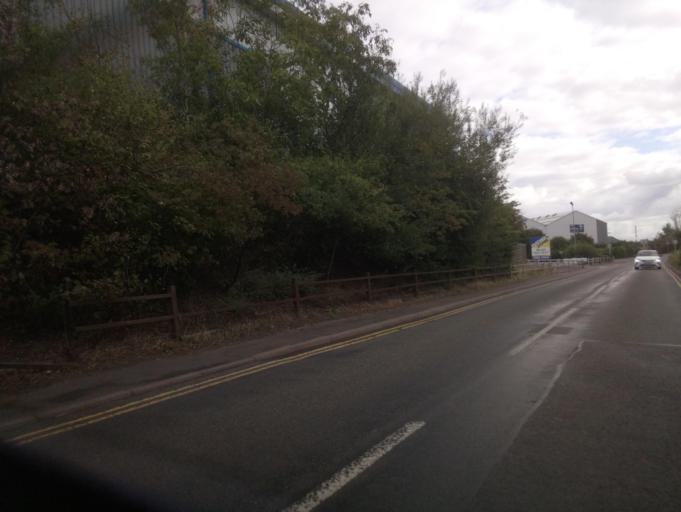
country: GB
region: England
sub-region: Leicestershire
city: Loughborough
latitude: 52.7846
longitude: -1.2014
